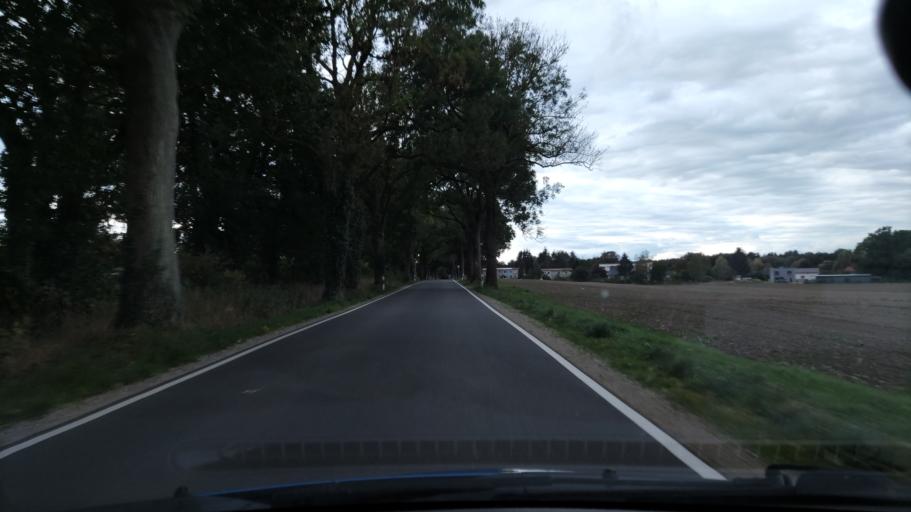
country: DE
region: Mecklenburg-Vorpommern
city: Zarrentin
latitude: 53.4621
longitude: 10.9759
